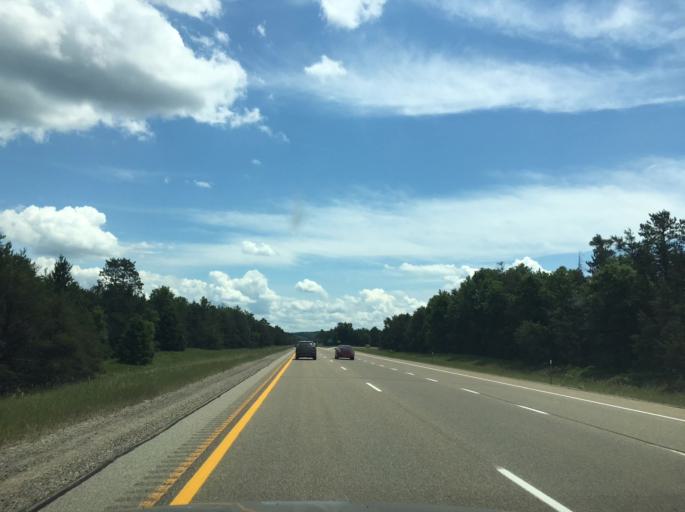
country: US
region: Michigan
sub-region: Roscommon County
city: Roscommon
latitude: 44.5172
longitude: -84.6663
